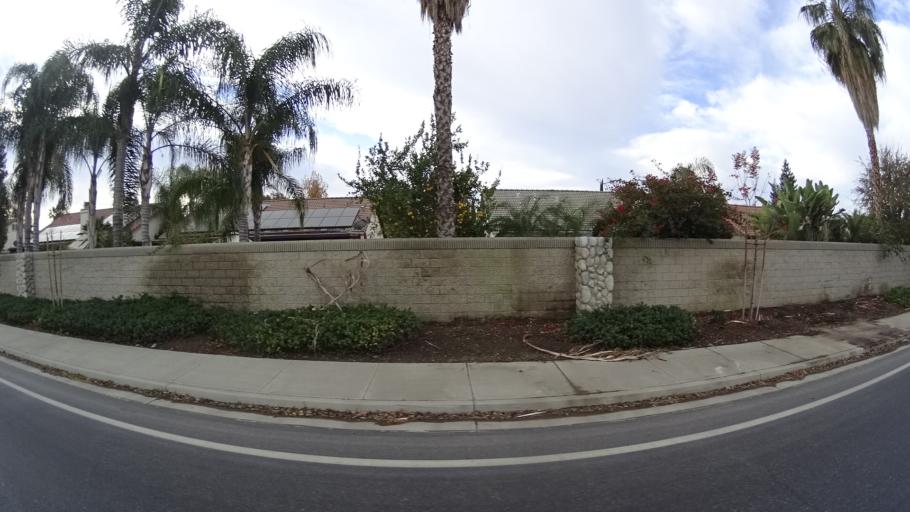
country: US
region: California
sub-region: Kern County
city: Greenacres
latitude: 35.4127
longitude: -119.0956
